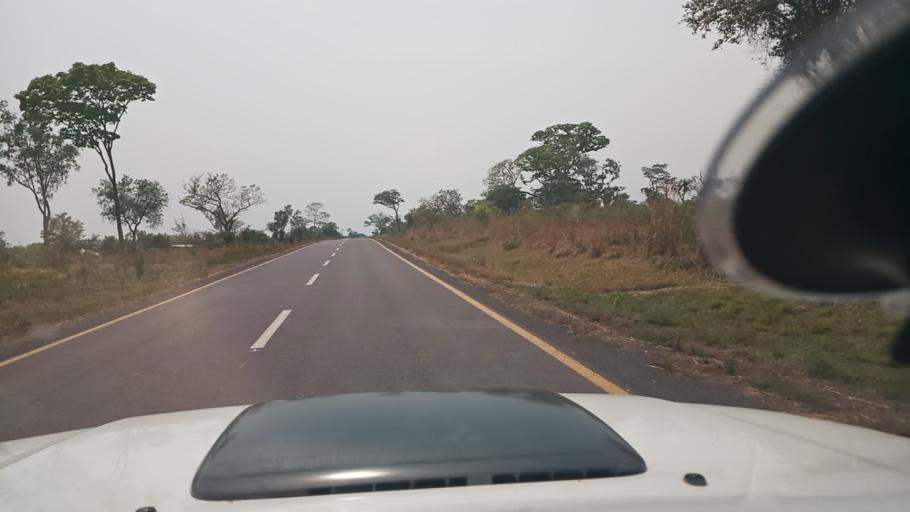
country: ZM
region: Luapula
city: Mansa
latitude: -10.9859
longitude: 28.1207
